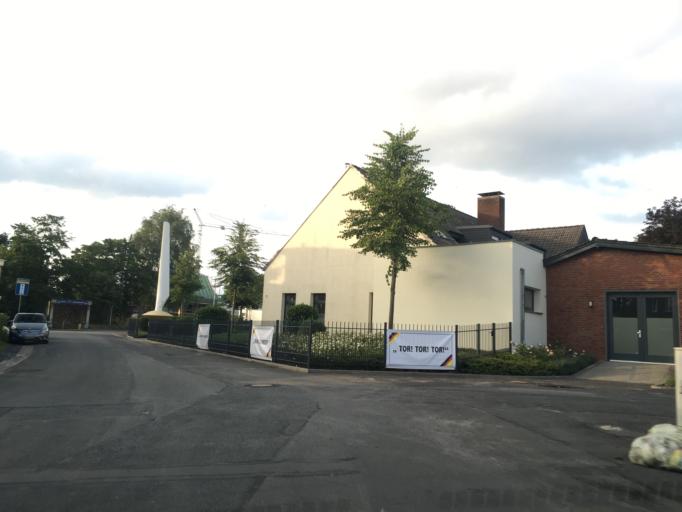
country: DE
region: North Rhine-Westphalia
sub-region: Regierungsbezirk Munster
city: Senden
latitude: 51.9137
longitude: 7.5275
